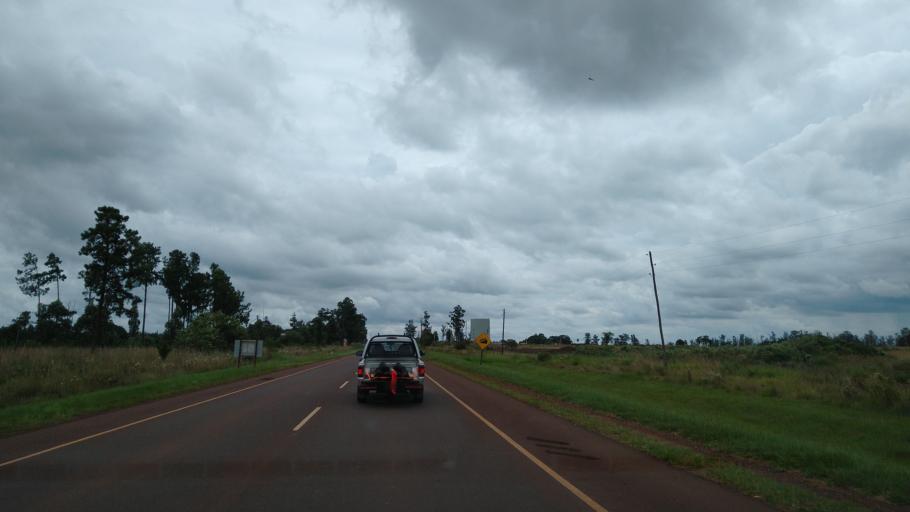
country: AR
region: Misiones
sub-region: Departamento de Capital
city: Posadas
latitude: -27.4176
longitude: -55.9886
